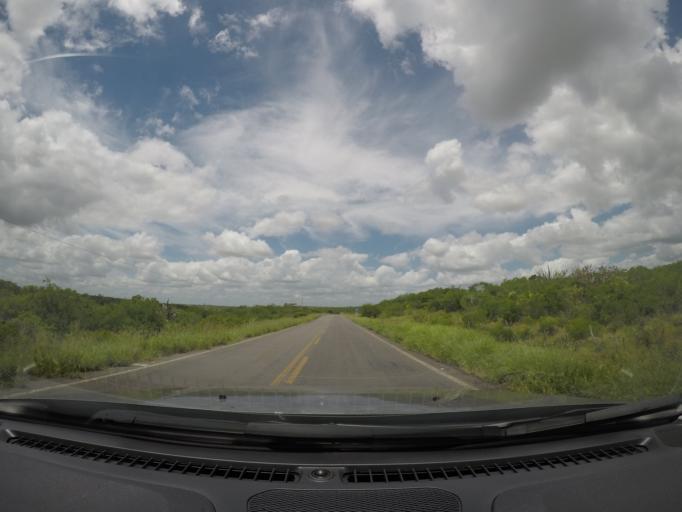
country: BR
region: Bahia
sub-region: Ipira
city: Ipira
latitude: -12.2867
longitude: -39.8709
